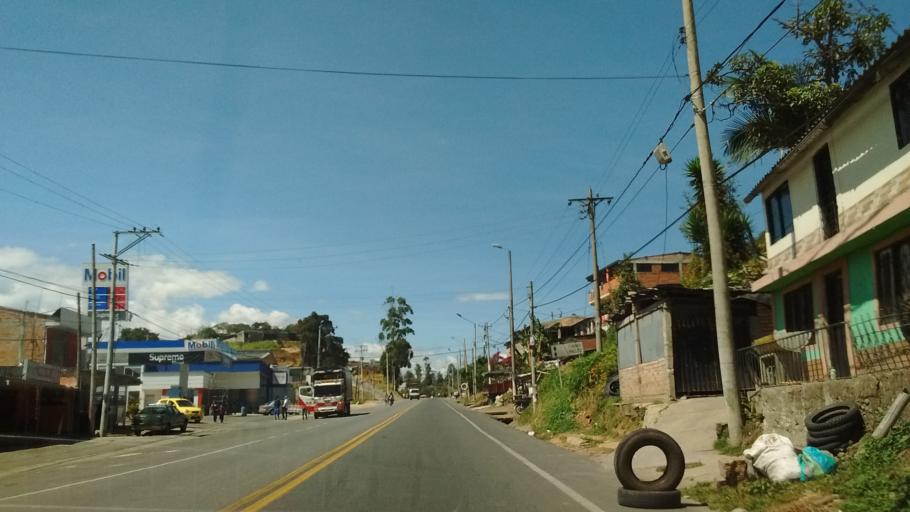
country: CO
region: Cauca
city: Popayan
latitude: 2.4292
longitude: -76.6211
